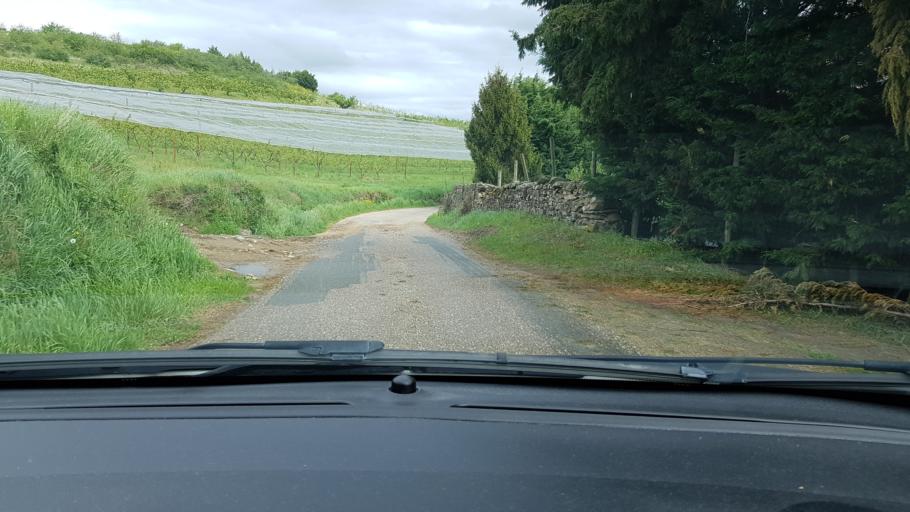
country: FR
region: Rhone-Alpes
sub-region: Departement du Rhone
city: Saint-Didier-sous-Riverie
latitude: 45.6058
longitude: 4.6231
